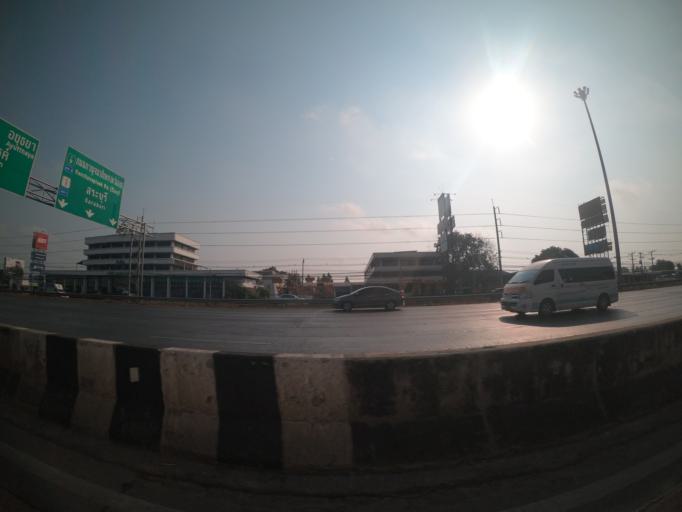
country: TH
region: Phra Nakhon Si Ayutthaya
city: Bang Pa-in
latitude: 14.1624
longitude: 100.6180
